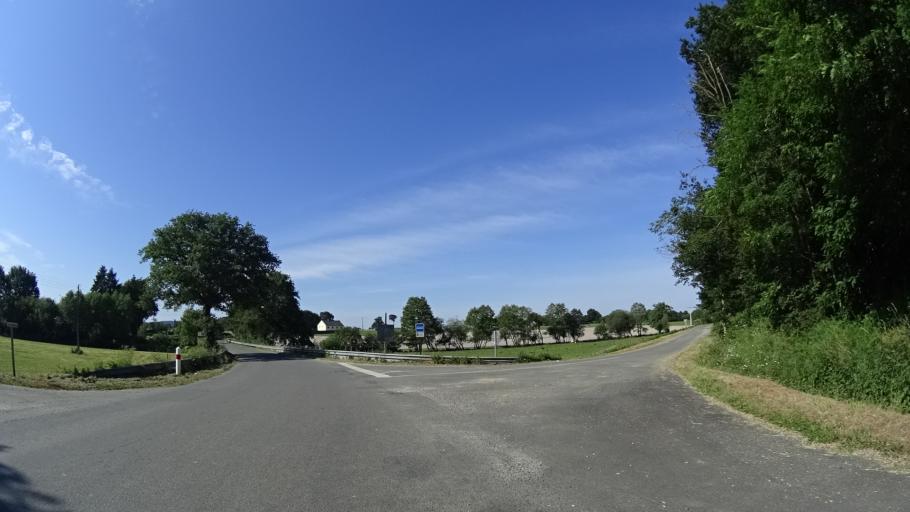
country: FR
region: Brittany
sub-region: Departement d'Ille-et-Vilaine
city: Guipry
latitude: 47.8129
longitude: -1.8506
